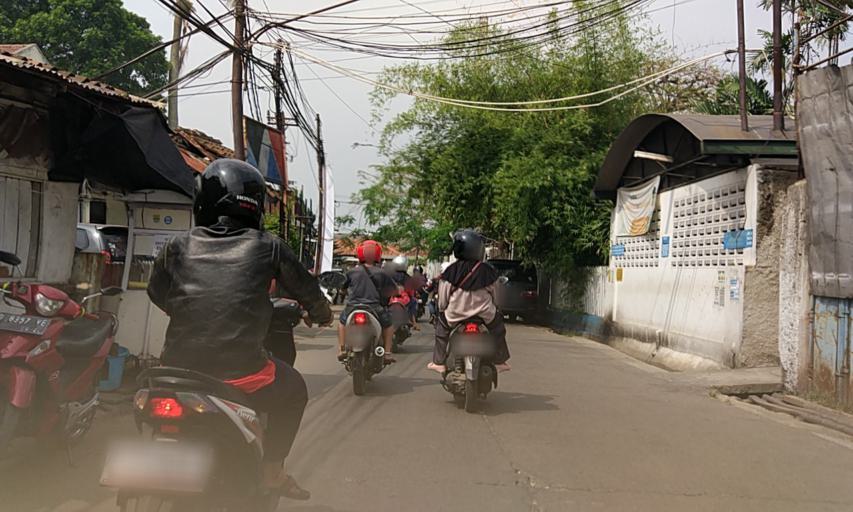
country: ID
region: West Java
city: Margahayukencana
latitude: -6.9404
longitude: 107.5831
